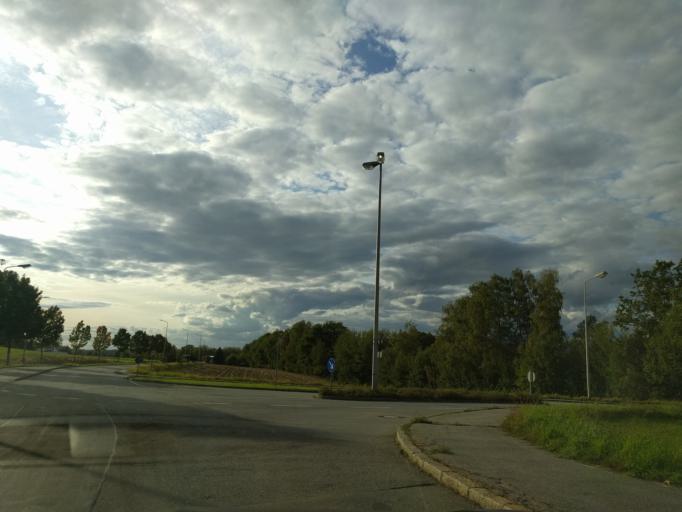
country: DE
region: Bavaria
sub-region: Lower Bavaria
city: Deggendorf
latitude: 48.8405
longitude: 12.9822
